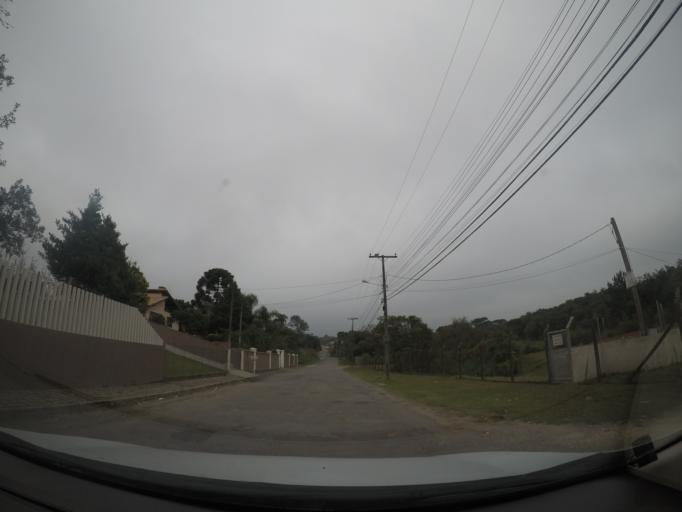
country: BR
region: Parana
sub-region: Colombo
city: Colombo
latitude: -25.3376
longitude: -49.2535
